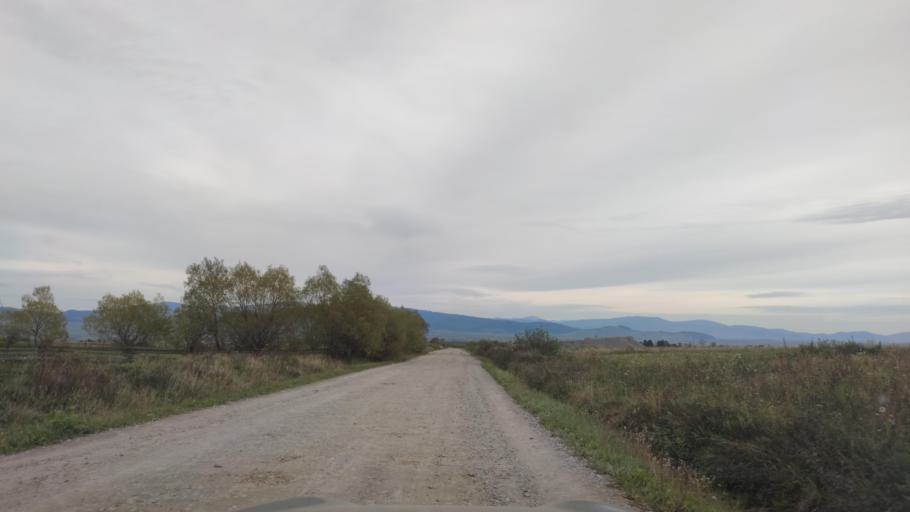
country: RO
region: Harghita
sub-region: Comuna Remetea
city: Remetea
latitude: 46.8091
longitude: 25.4013
